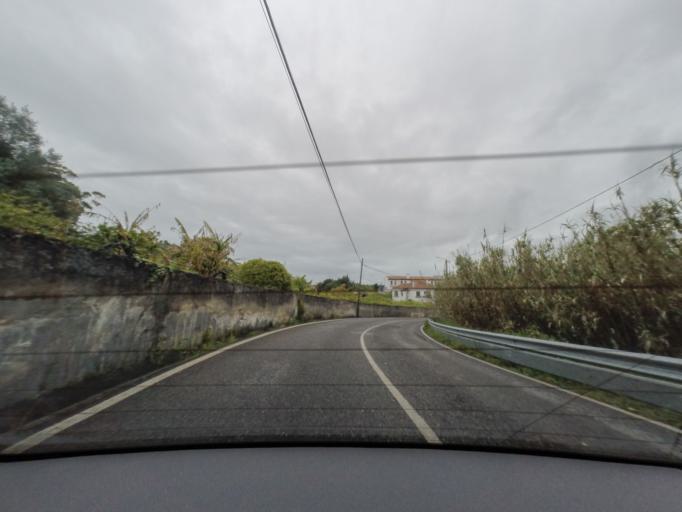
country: PT
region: Lisbon
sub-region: Sintra
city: Sintra
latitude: 38.8073
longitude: -9.3893
